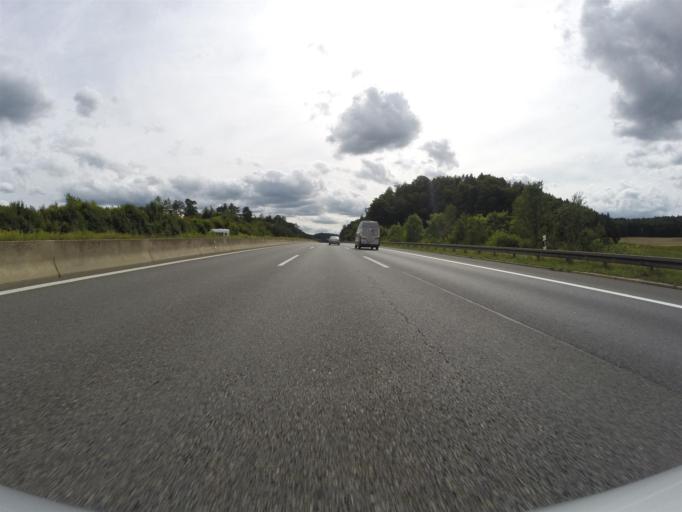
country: DE
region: Bavaria
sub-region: Regierungsbezirk Mittelfranken
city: Velden
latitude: 49.6595
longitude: 11.4620
